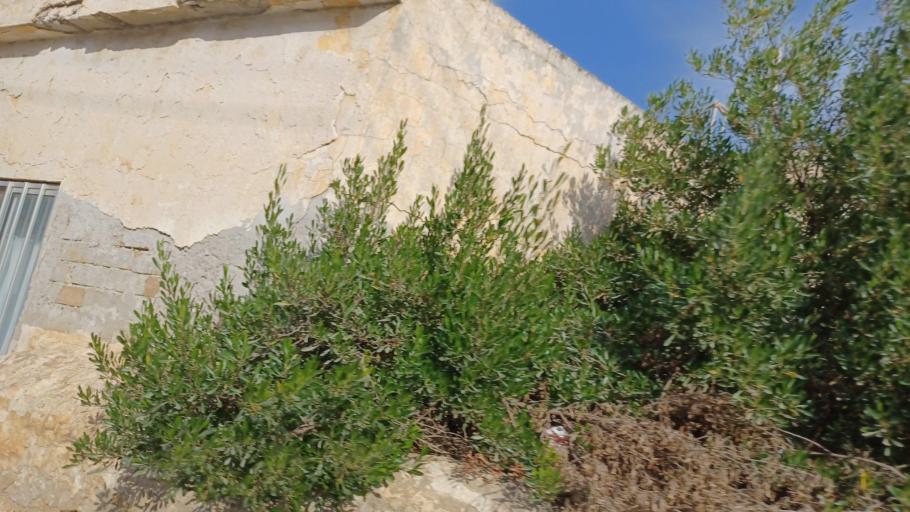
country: CY
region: Ammochostos
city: Frenaros
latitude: 35.0420
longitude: 33.9216
